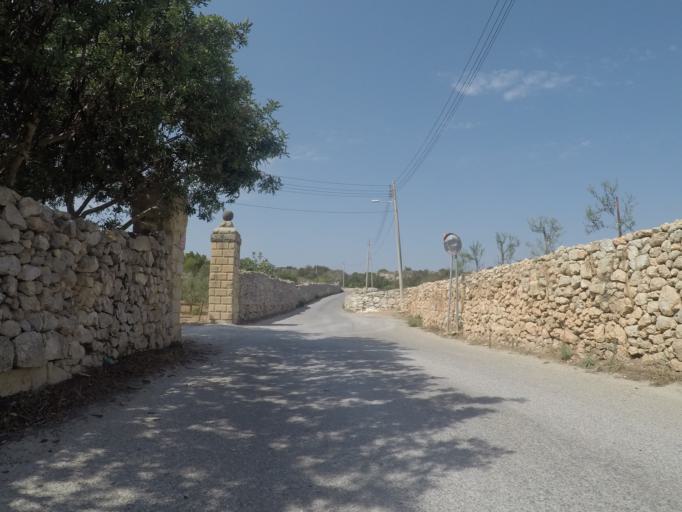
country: MT
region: L-Imgarr
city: Imgarr
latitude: 35.9347
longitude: 14.3787
